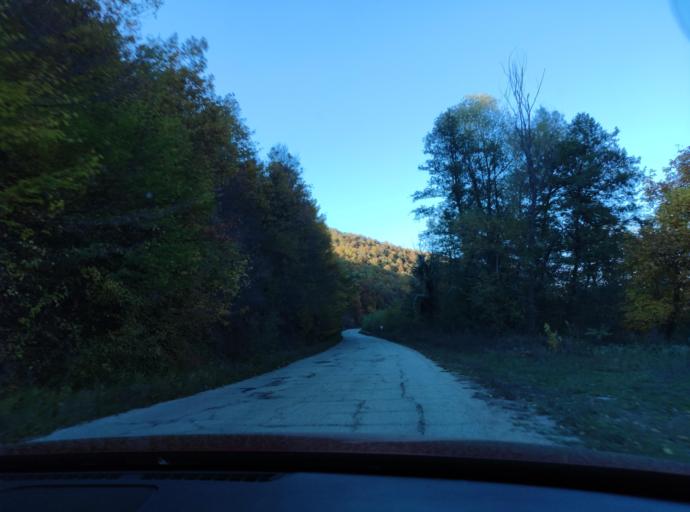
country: BG
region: Montana
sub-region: Obshtina Chiprovtsi
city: Chiprovtsi
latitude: 43.4088
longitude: 22.9387
